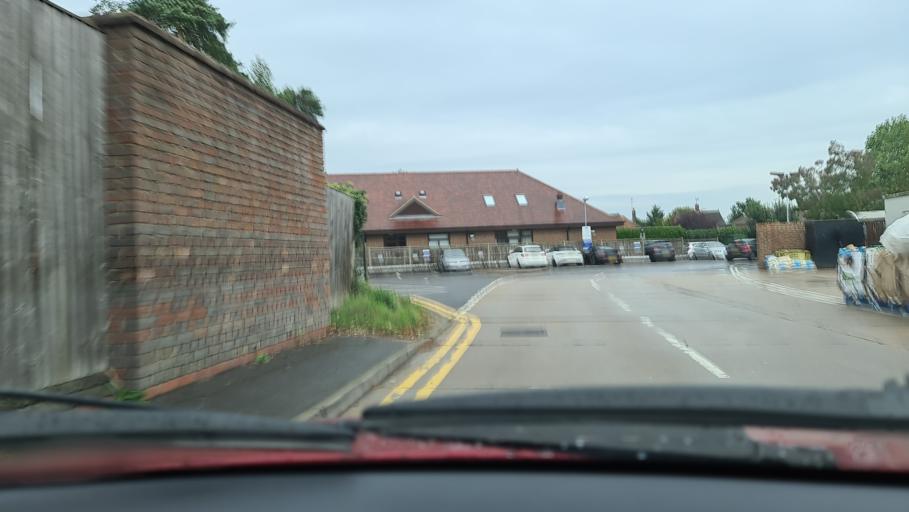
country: GB
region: England
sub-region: Buckinghamshire
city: Beaconsfield
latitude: 51.6124
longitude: -0.6456
